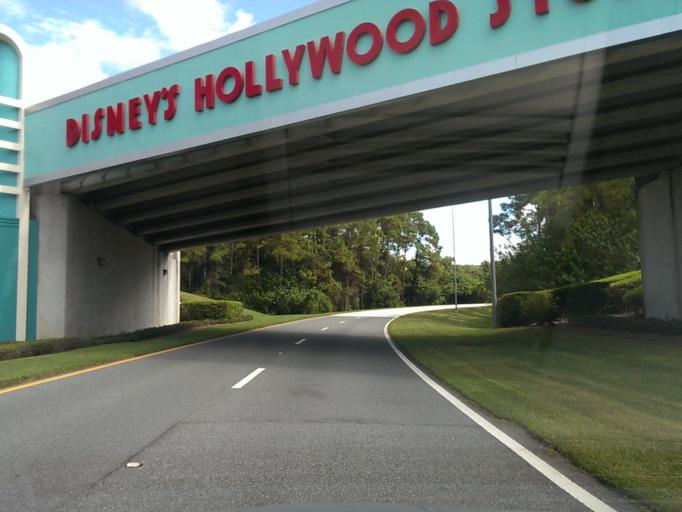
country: US
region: Florida
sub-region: Osceola County
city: Celebration
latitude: 28.3508
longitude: -81.5641
